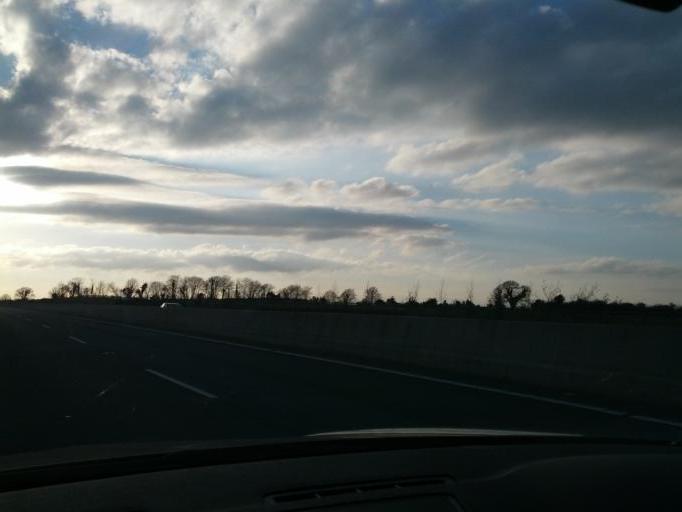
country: IE
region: Munster
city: Nenagh Bridge
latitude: 52.8740
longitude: -8.0399
